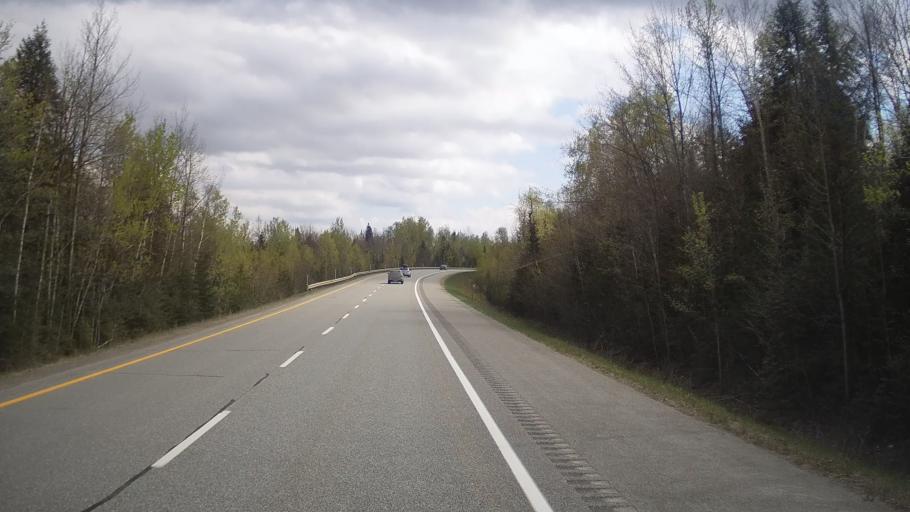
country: CA
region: Quebec
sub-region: Estrie
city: Magog
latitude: 45.1551
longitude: -72.0662
